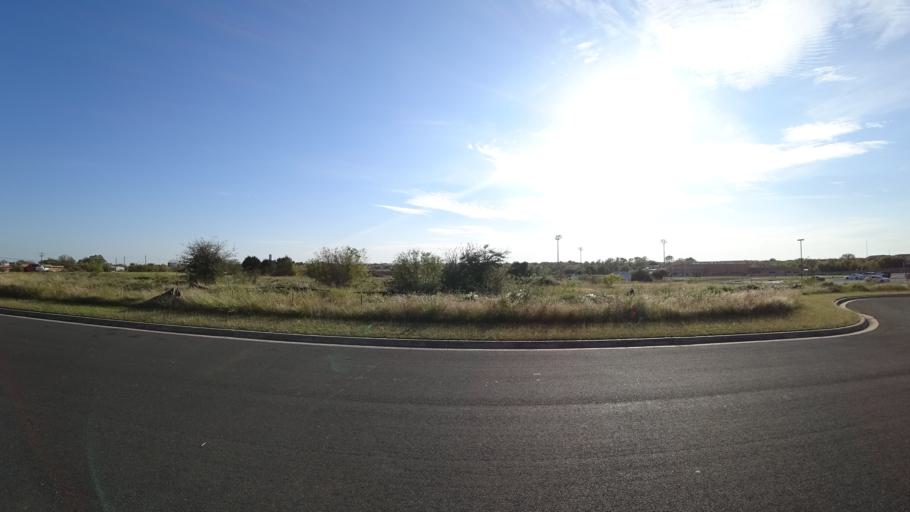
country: US
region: Texas
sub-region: Travis County
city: Pflugerville
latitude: 30.4010
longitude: -97.6425
